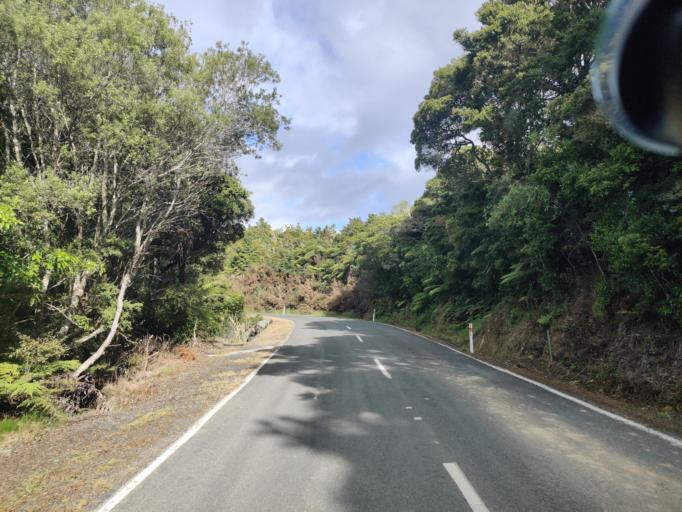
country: NZ
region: Northland
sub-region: Whangarei
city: Ngunguru
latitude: -35.5843
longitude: 174.4285
